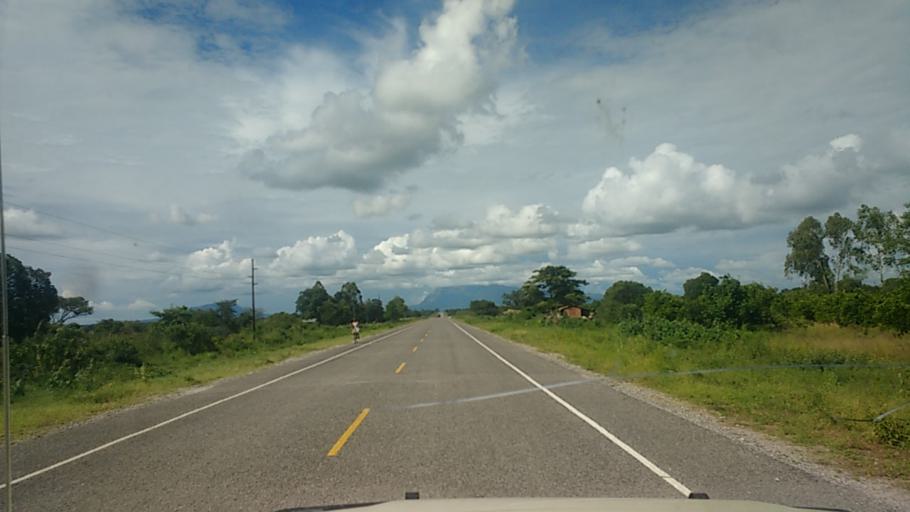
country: UG
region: Eastern Region
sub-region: Katakwi District
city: Katakwi
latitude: 1.9207
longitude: 34.0498
